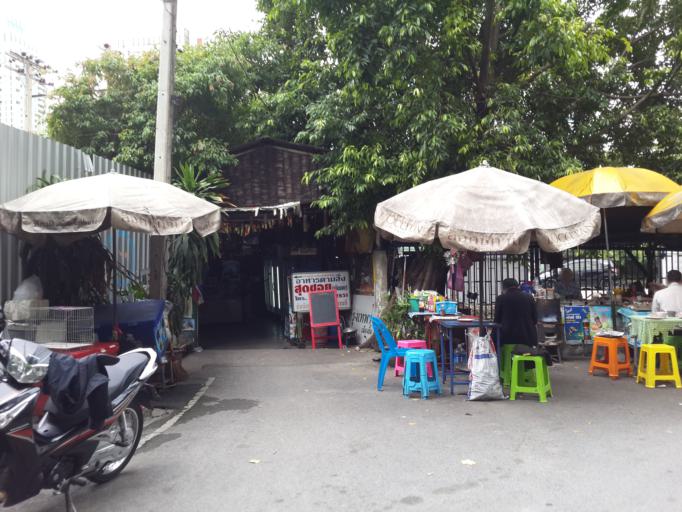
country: TH
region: Bangkok
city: Ratchathewi
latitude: 13.7460
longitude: 100.5422
